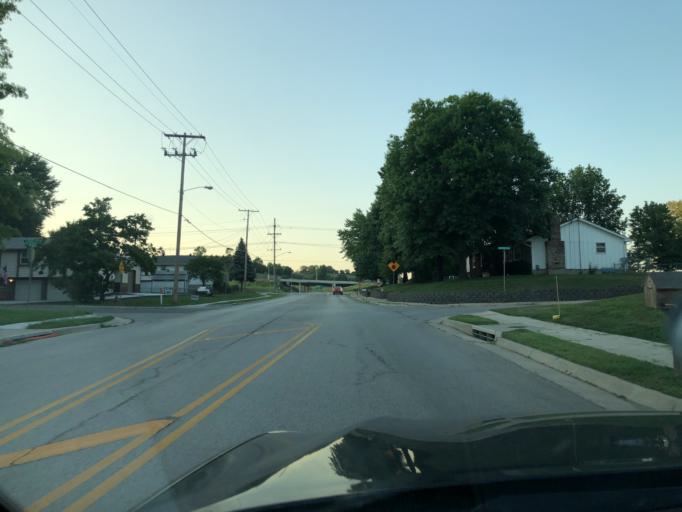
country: US
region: Kansas
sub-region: Leavenworth County
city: Leavenworth
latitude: 39.3257
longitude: -94.9506
